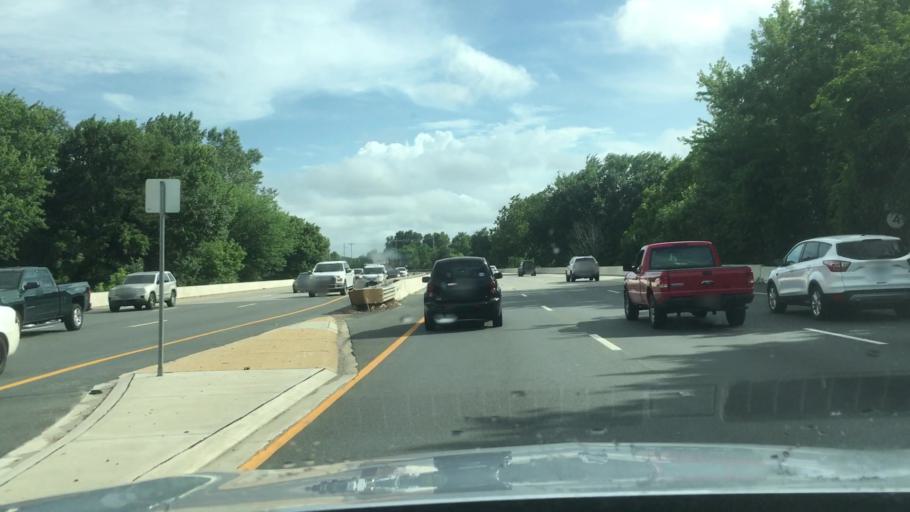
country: US
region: Delaware
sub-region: New Castle County
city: Newport
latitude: 39.7081
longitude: -75.6529
